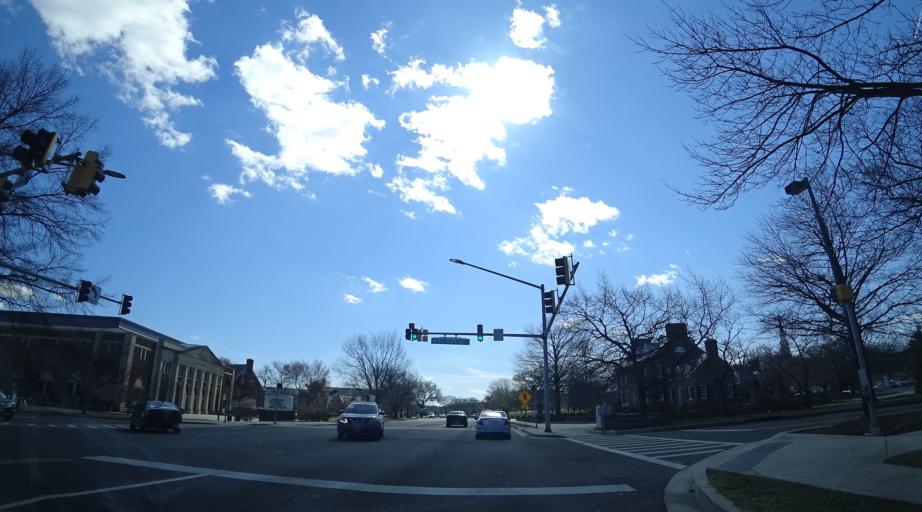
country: US
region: Maryland
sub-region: Prince George's County
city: College Park
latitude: 38.9859
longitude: -76.9370
